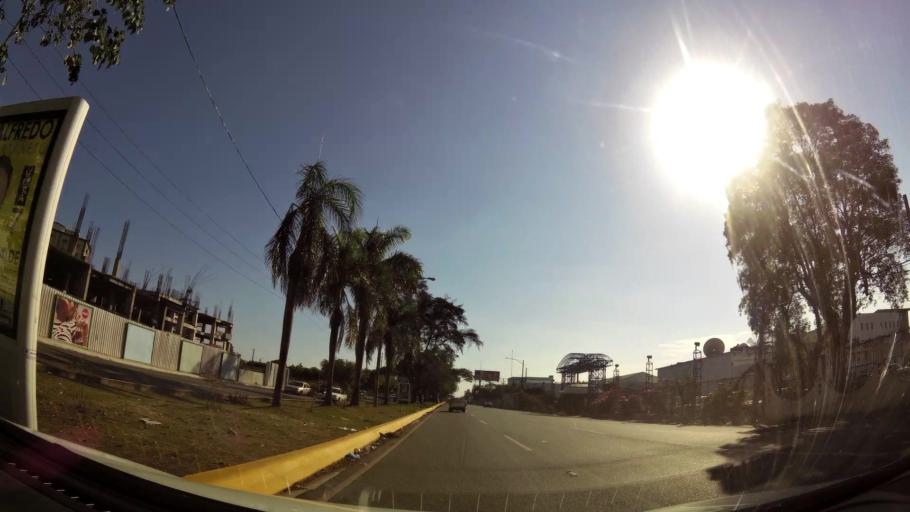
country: DO
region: Nacional
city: Bella Vista
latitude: 18.4381
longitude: -69.9811
